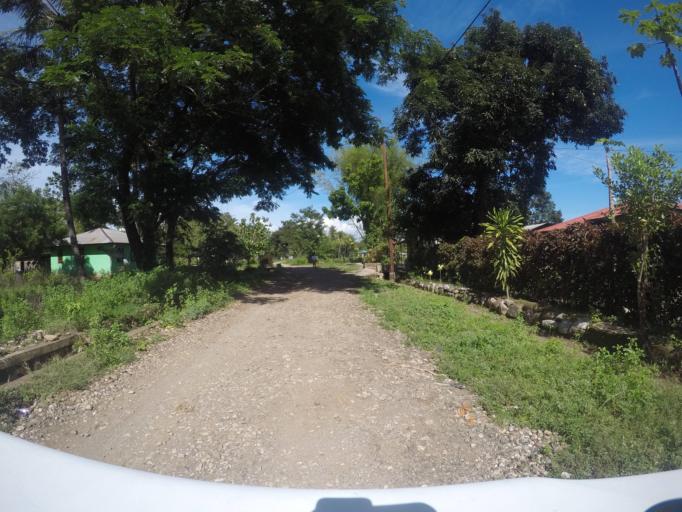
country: TL
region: Bobonaro
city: Maliana
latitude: -8.9877
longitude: 125.1980
